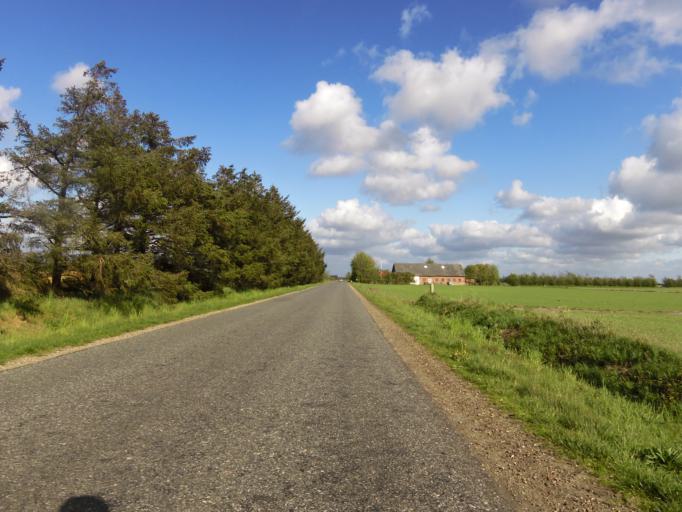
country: DK
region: South Denmark
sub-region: Esbjerg Kommune
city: Ribe
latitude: 55.2605
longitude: 8.7752
